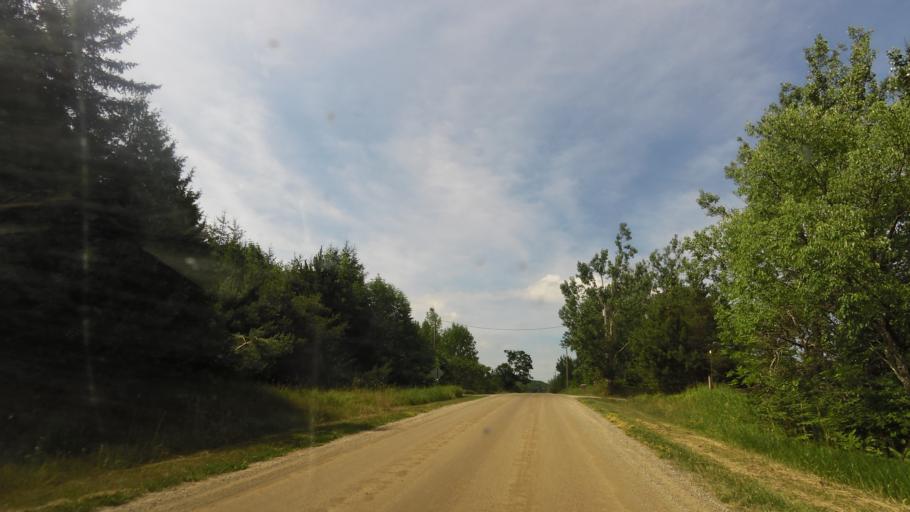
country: CA
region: Ontario
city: Orangeville
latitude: 43.9988
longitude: -80.0493
